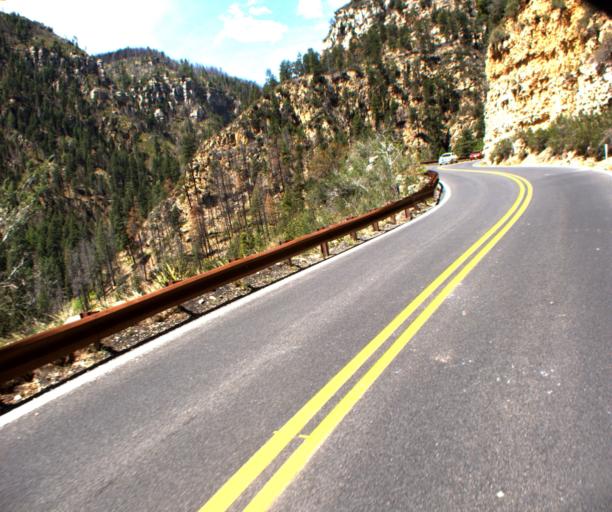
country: US
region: Arizona
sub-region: Coconino County
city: Kachina Village
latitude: 35.0261
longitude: -111.7393
